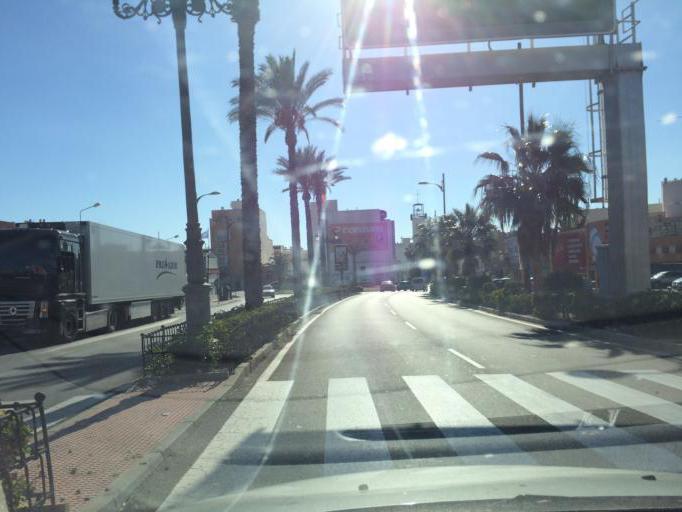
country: ES
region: Andalusia
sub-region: Provincia de Almeria
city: Aguadulce
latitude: 36.8101
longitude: -2.5975
